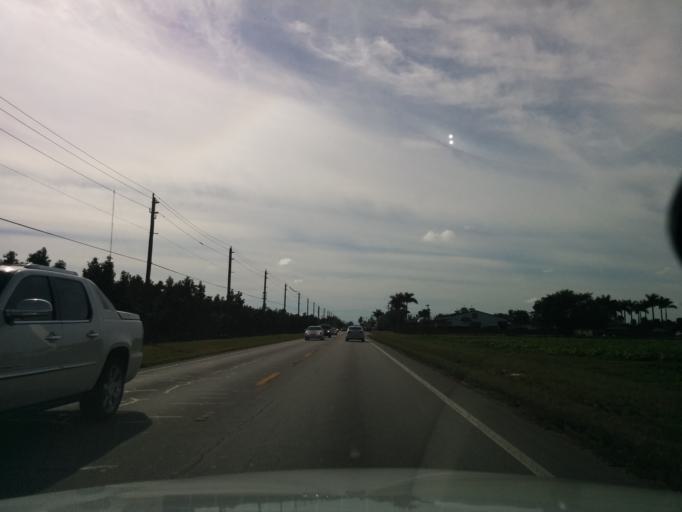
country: US
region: Florida
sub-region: Miami-Dade County
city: Richmond West
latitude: 25.5609
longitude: -80.4781
